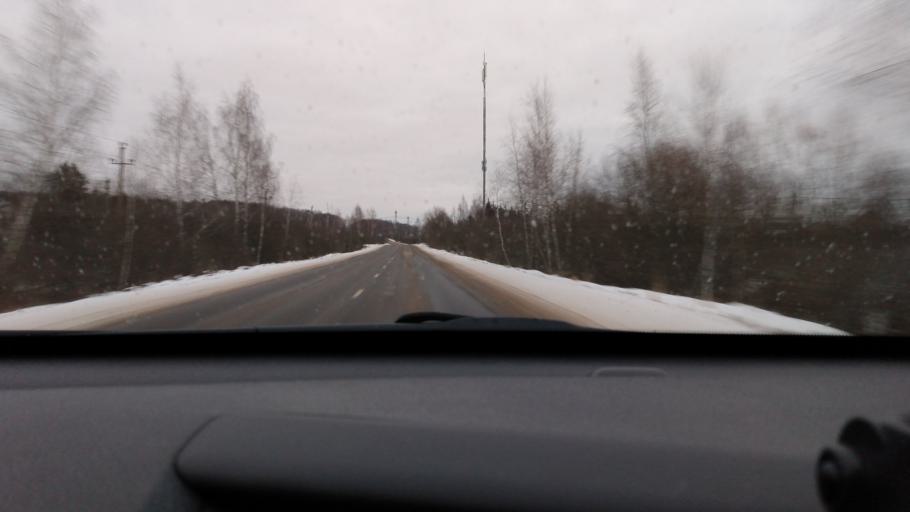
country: RU
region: Moskovskaya
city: Bronnitsy
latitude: 55.2904
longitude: 38.2459
